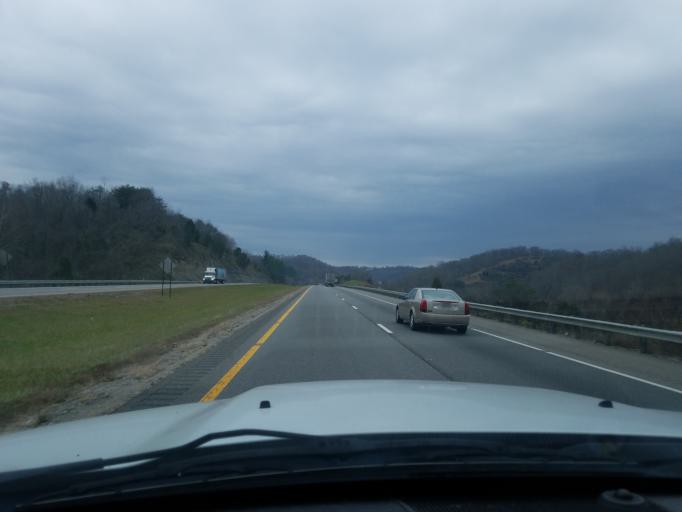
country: US
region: Kentucky
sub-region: Boyd County
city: Catlettsburg
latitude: 38.3807
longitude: -82.6185
